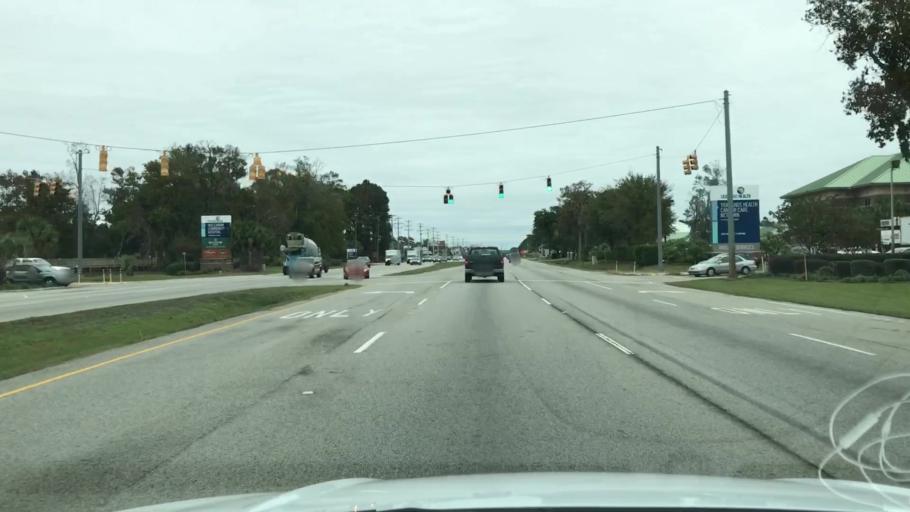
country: US
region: South Carolina
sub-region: Georgetown County
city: Murrells Inlet
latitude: 33.5584
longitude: -79.0421
